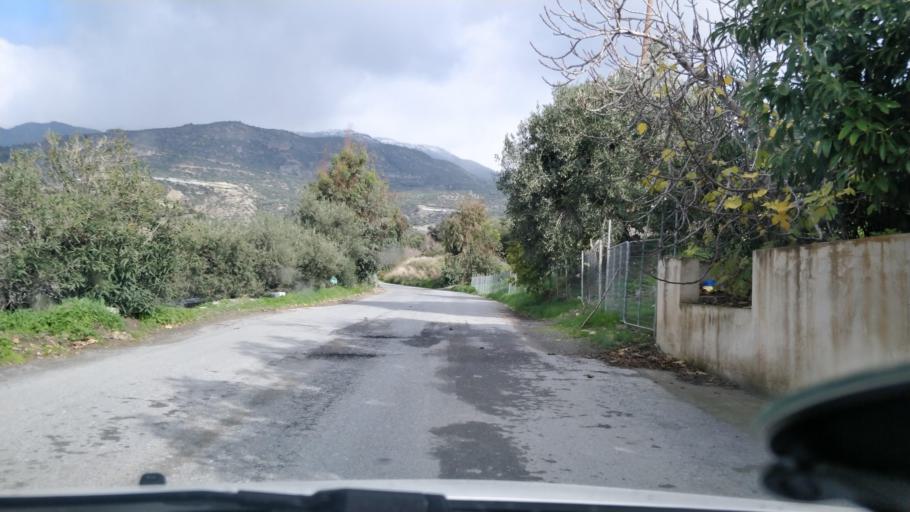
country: GR
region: Crete
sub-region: Nomos Lasithiou
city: Gra Liyia
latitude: 34.9869
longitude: 25.4997
